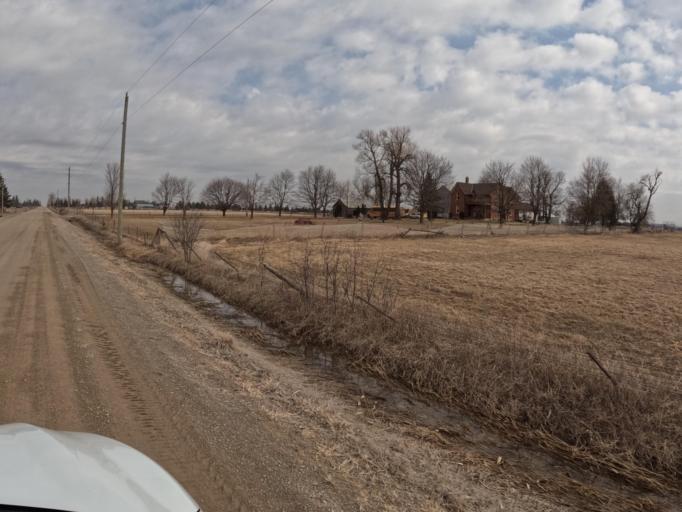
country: CA
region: Ontario
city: Orangeville
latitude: 43.9013
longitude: -80.2133
